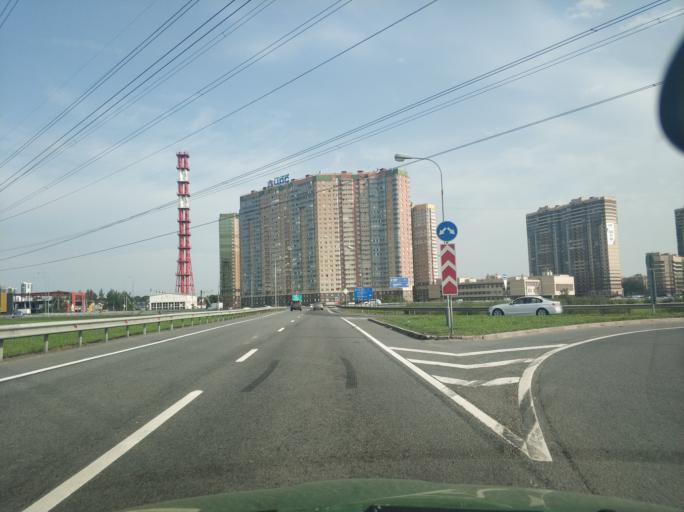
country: RU
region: Leningrad
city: Murino
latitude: 60.0386
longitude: 30.4430
